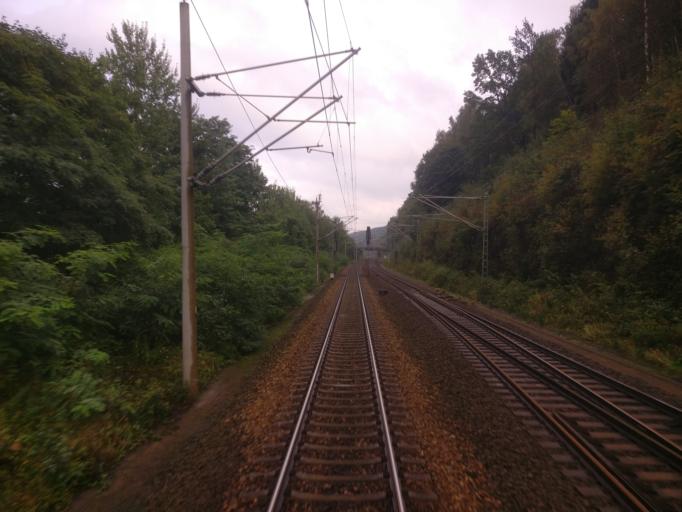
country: DE
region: Saxony
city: Bad Schandau
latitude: 50.9172
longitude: 14.1456
